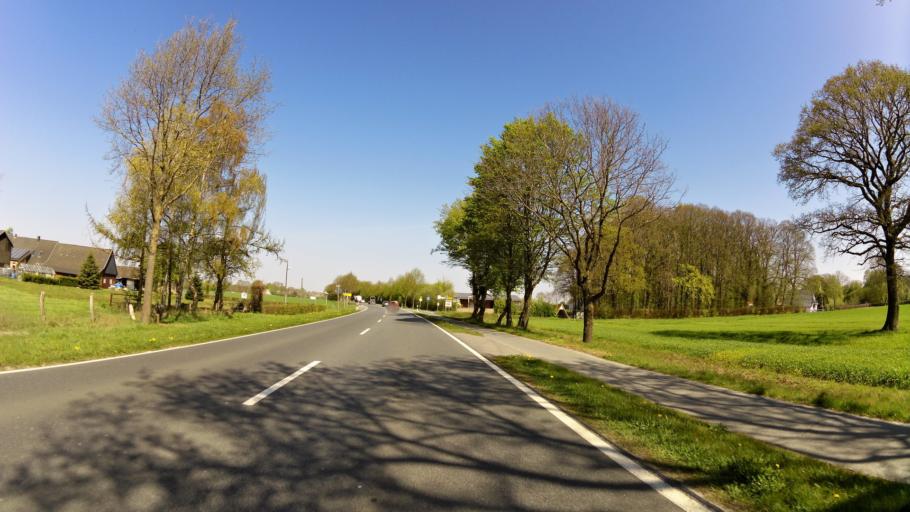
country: DE
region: Lower Saxony
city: Ganderkesee
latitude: 53.0684
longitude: 8.5287
